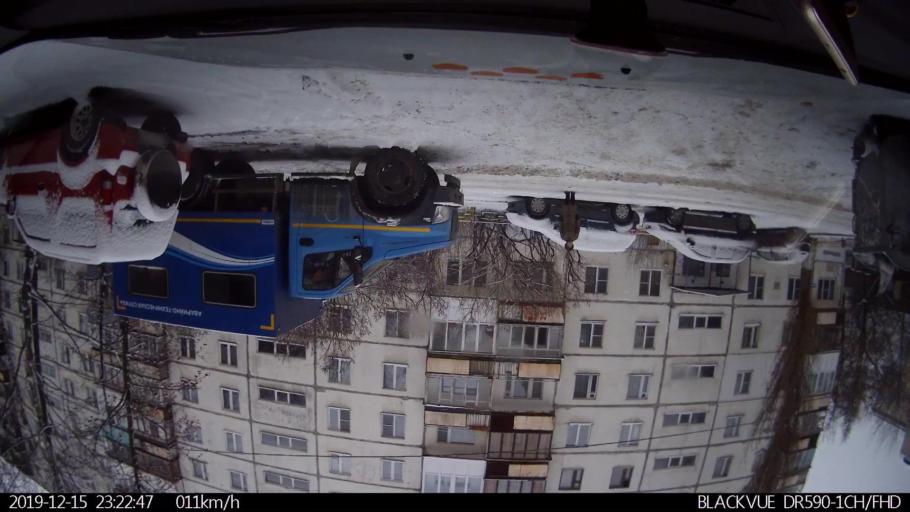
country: RU
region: Nizjnij Novgorod
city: Gorbatovka
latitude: 56.3573
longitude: 43.7625
